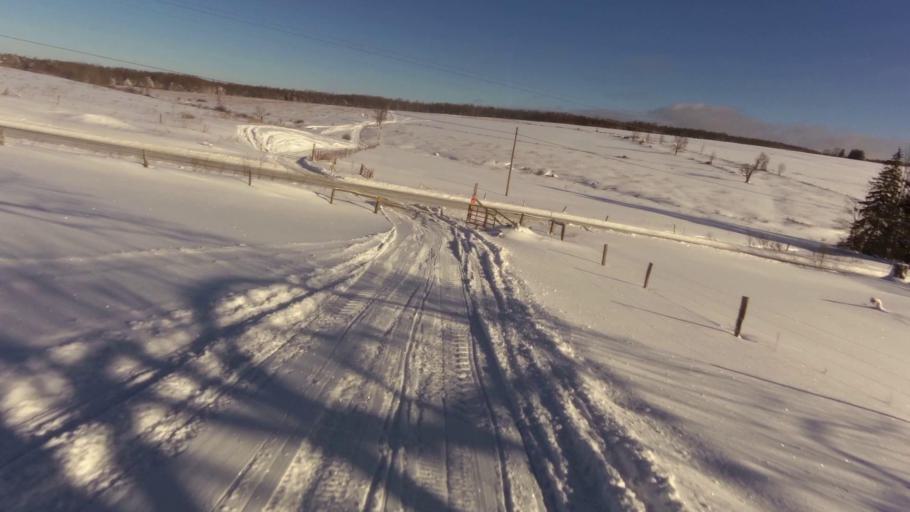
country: US
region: New York
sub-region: Chautauqua County
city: Falconer
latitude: 42.2607
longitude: -79.2030
